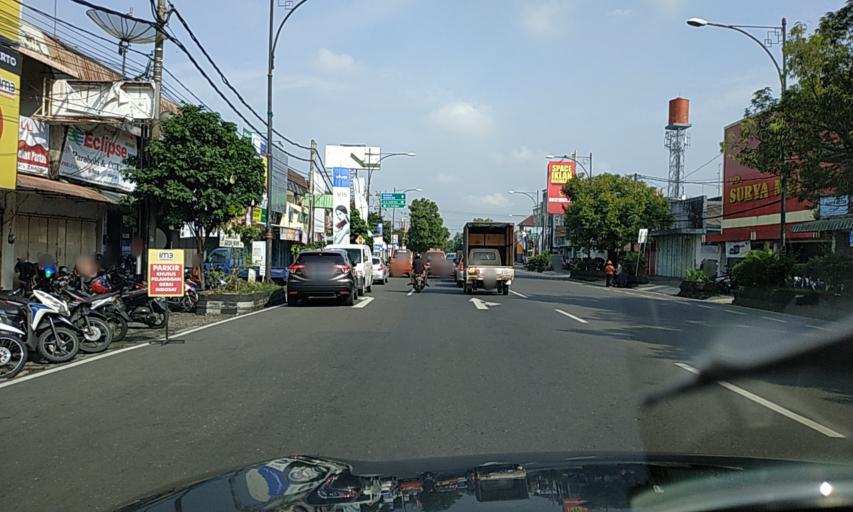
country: ID
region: Central Java
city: Purwokerto
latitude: -7.4266
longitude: 109.2358
